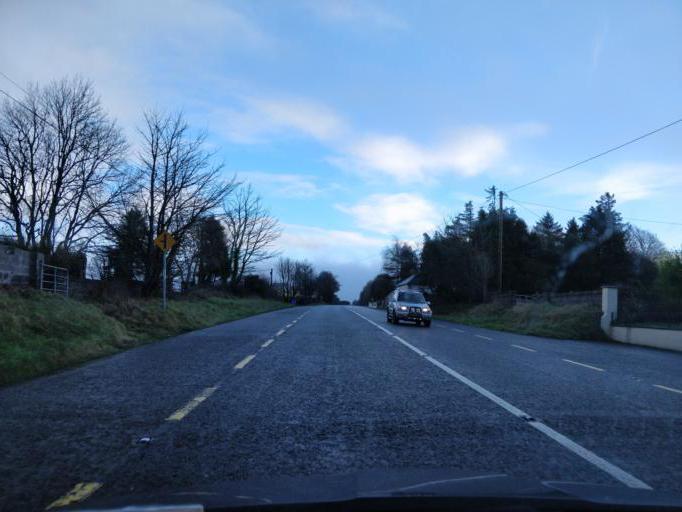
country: IE
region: Connaught
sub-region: Maigh Eo
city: Foxford
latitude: 53.8968
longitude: -9.0946
